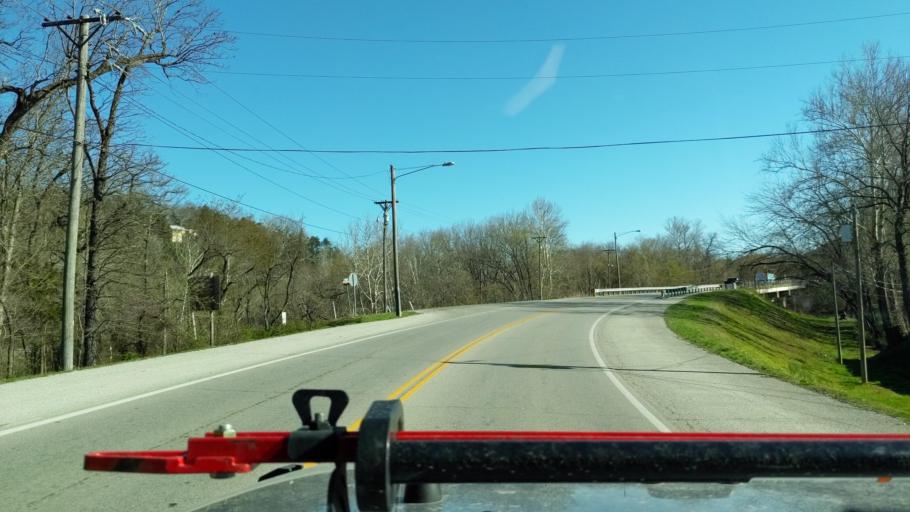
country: US
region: Missouri
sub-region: Taney County
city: Hollister
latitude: 36.6272
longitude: -93.2195
